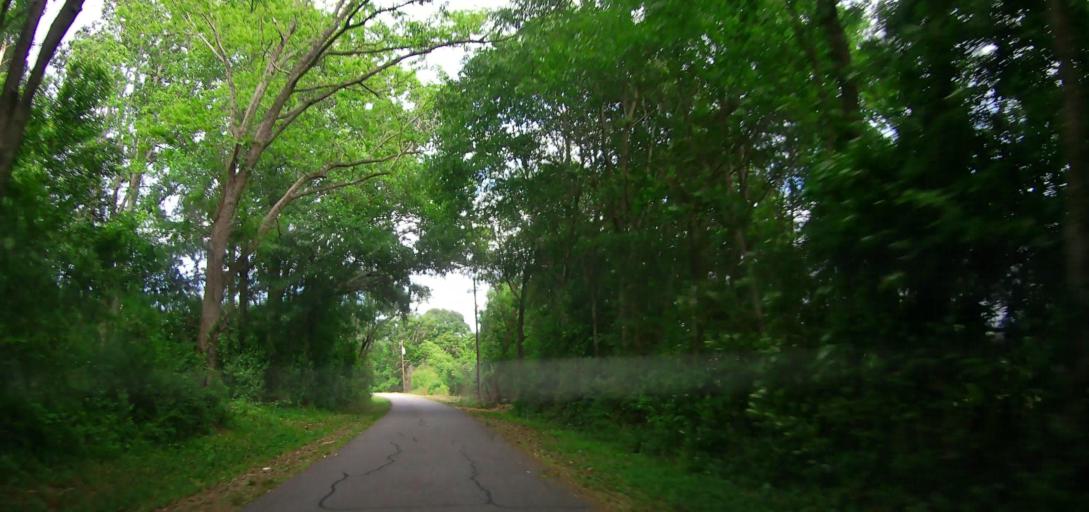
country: US
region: Georgia
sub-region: Oconee County
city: Watkinsville
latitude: 33.8211
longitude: -83.4425
